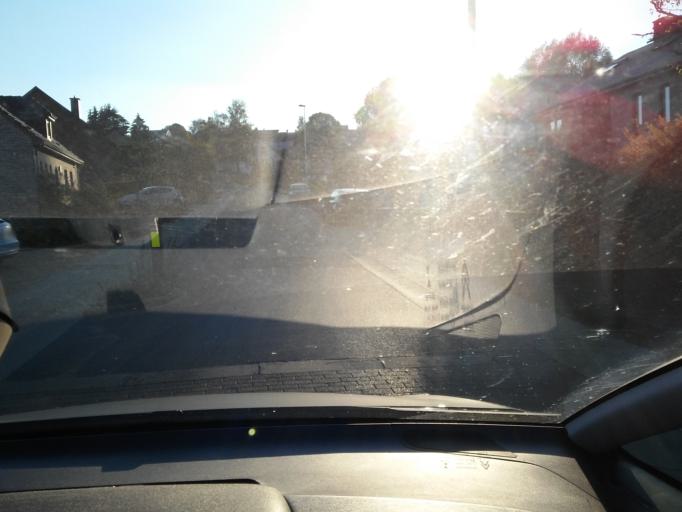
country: BE
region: Wallonia
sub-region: Province du Luxembourg
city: Arlon
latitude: 49.6934
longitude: 5.8271
